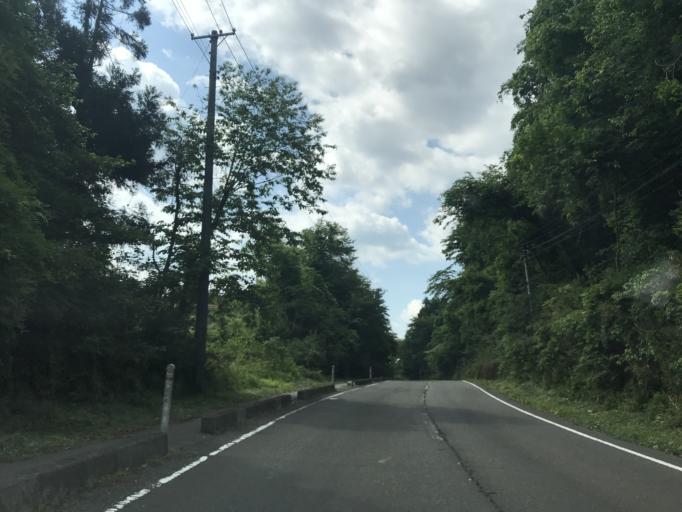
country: JP
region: Miyagi
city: Furukawa
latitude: 38.7723
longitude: 140.9627
